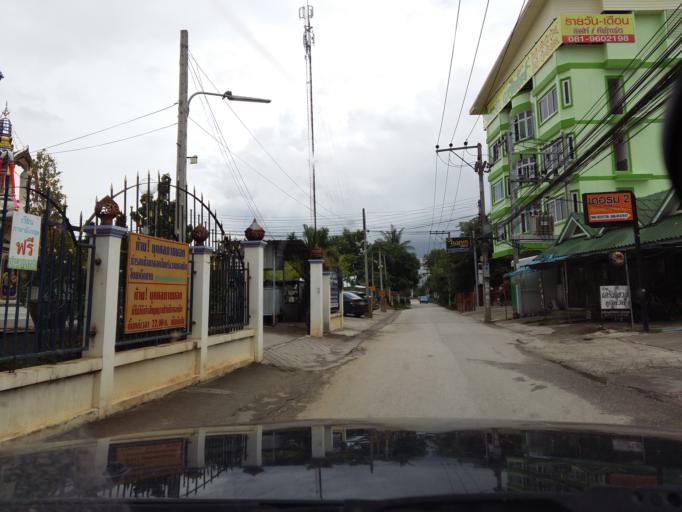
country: TH
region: Chiang Mai
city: Chiang Mai
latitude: 18.7560
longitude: 98.9726
